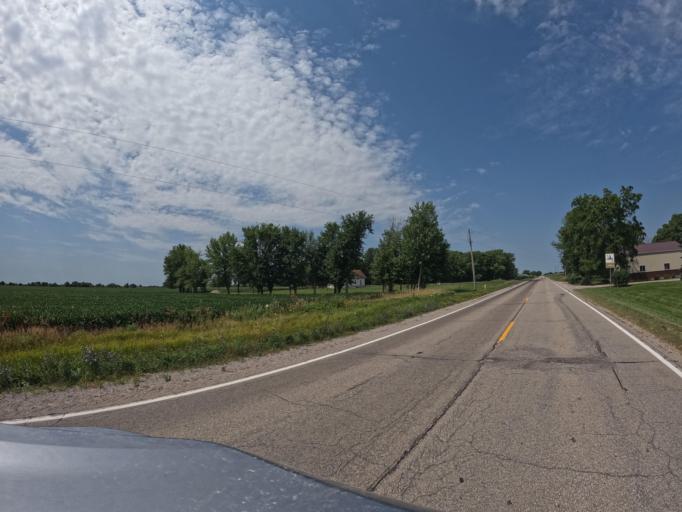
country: US
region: Iowa
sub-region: Appanoose County
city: Centerville
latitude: 40.8123
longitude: -92.9433
